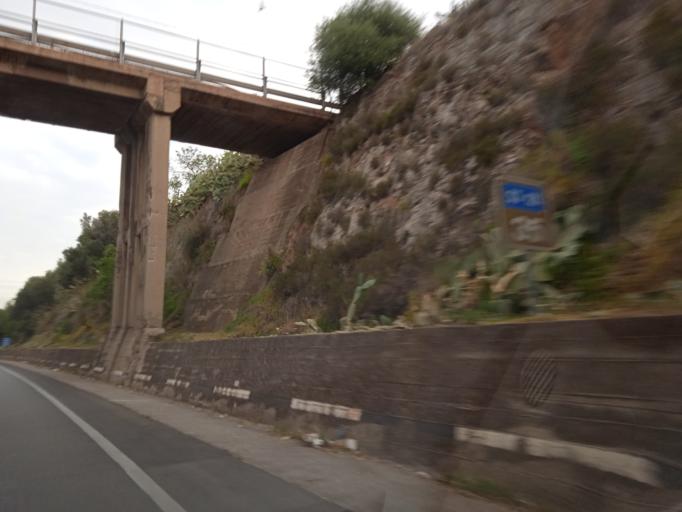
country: IT
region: Sicily
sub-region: Palermo
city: Portella di Mare
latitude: 38.0622
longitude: 13.4619
